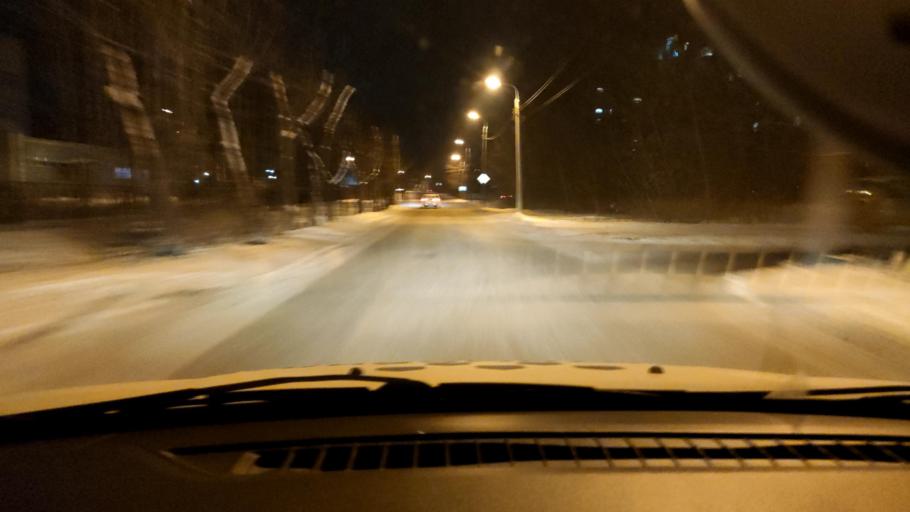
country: RU
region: Perm
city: Overyata
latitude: 58.0116
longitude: 55.9599
